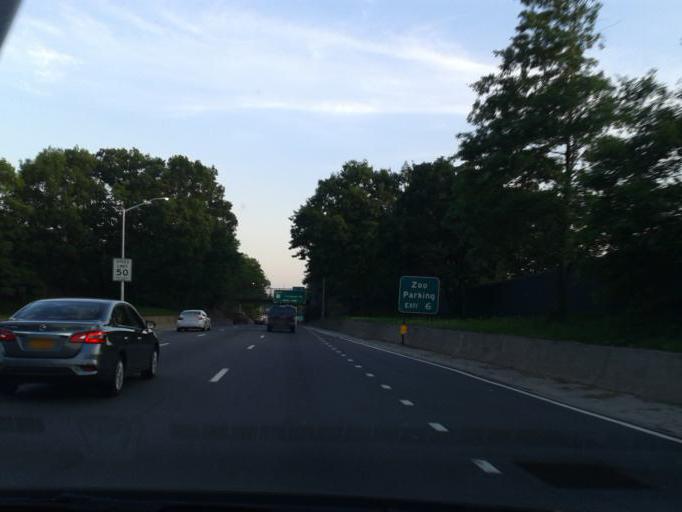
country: US
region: New York
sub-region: Bronx
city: The Bronx
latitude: 40.8630
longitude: -73.8721
